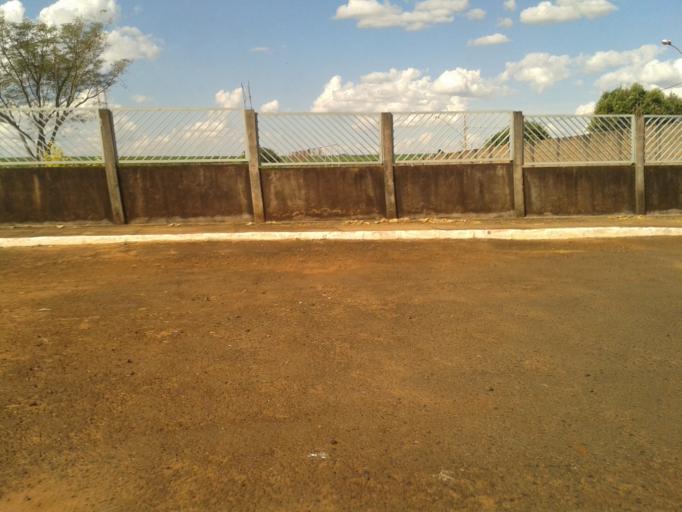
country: BR
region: Minas Gerais
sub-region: Santa Vitoria
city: Santa Vitoria
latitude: -18.6932
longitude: -49.9388
